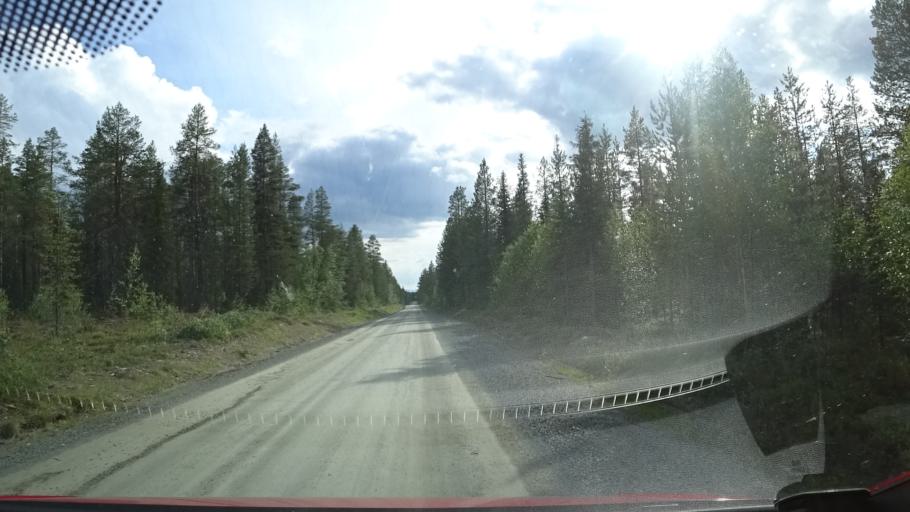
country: FI
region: Lapland
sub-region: Tunturi-Lappi
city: Kittilae
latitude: 67.9552
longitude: 25.0910
